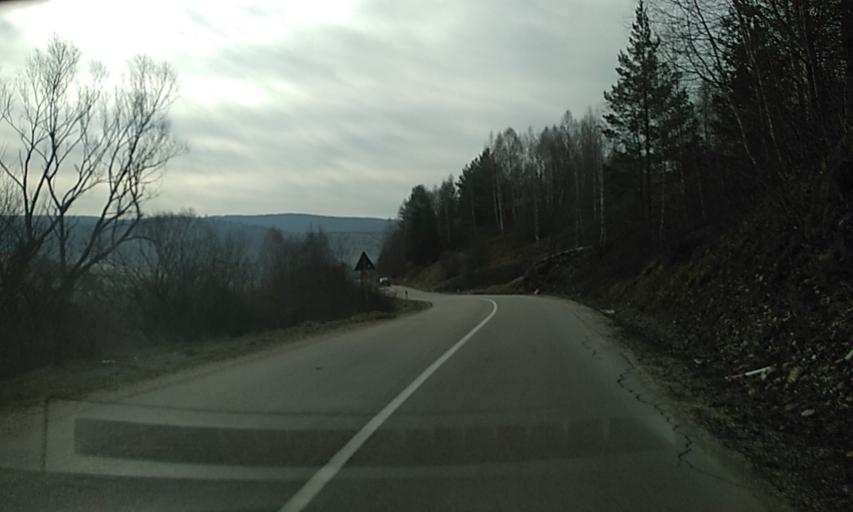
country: RS
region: Central Serbia
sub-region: Pcinjski Okrug
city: Bosilegrad
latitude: 42.6327
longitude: 22.3873
